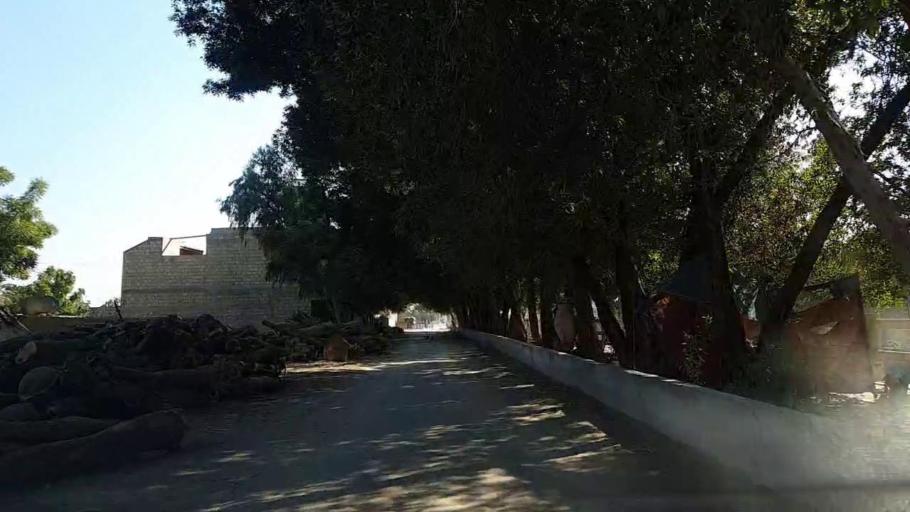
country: PK
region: Sindh
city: Nawabshah
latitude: 26.2452
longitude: 68.4219
